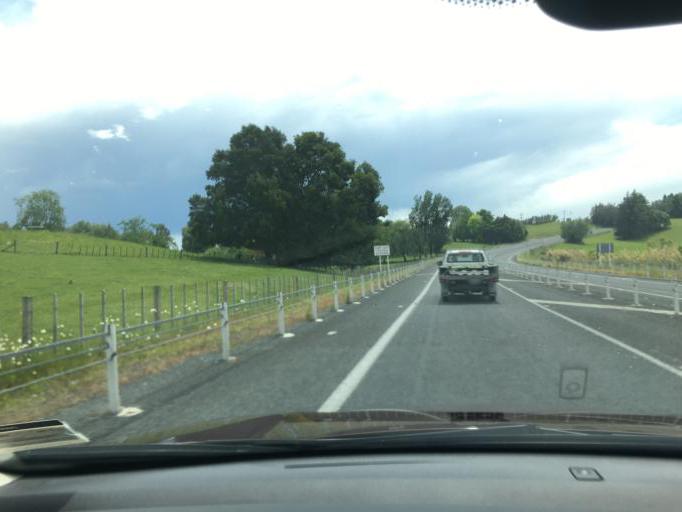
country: NZ
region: Waikato
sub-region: Waipa District
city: Cambridge
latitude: -37.9523
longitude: 175.3156
